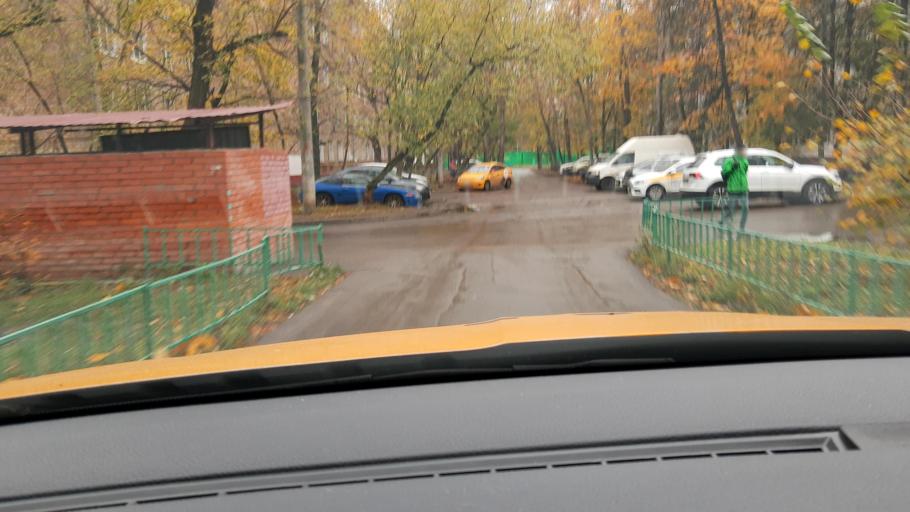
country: RU
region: Moscow
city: Novokuz'minki
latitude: 55.7020
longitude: 37.7714
